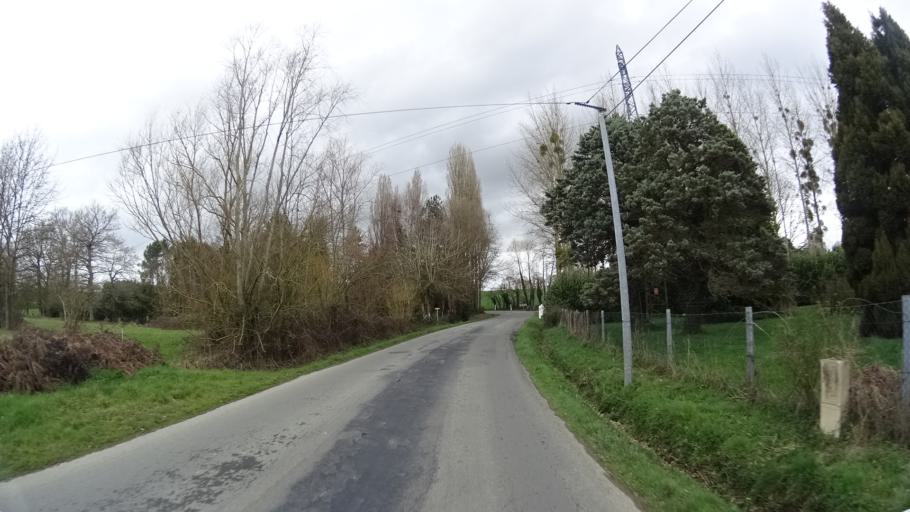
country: FR
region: Brittany
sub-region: Departement d'Ille-et-Vilaine
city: Saint-Gilles
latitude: 48.1701
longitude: -1.8292
